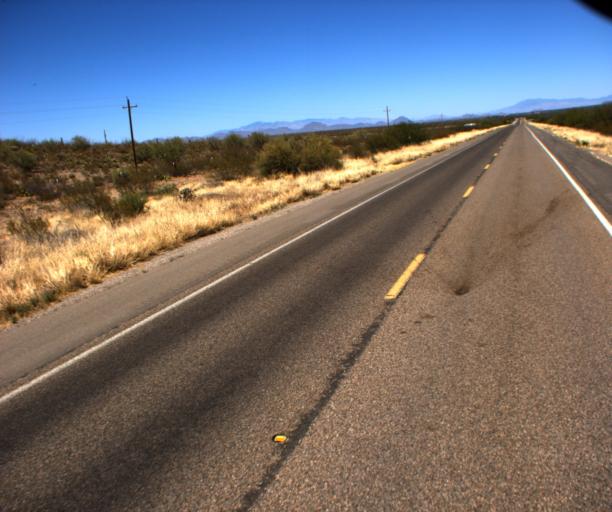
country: US
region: Arizona
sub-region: Pima County
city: Three Points
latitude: 32.0631
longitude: -111.3832
